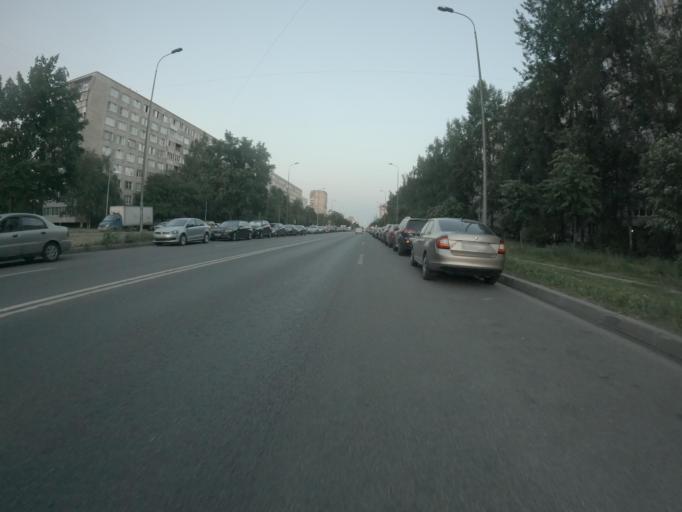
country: RU
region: St.-Petersburg
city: Krasnogvargeisky
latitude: 59.9205
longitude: 30.4799
